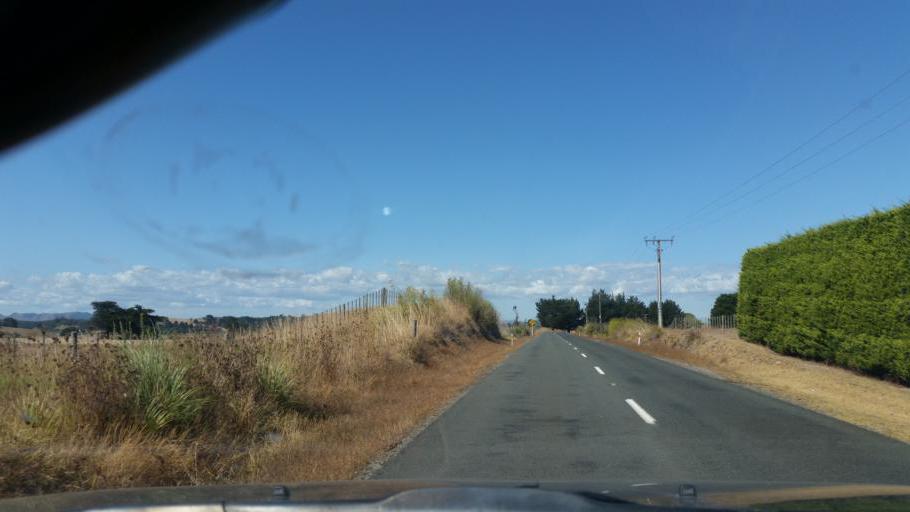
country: NZ
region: Northland
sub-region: Kaipara District
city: Dargaville
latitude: -35.9442
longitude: 173.8220
